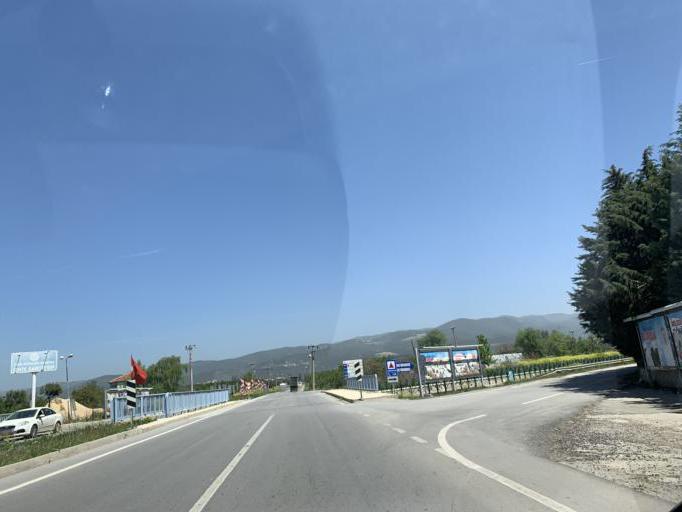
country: TR
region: Bursa
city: Iznik
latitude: 40.4116
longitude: 29.7088
